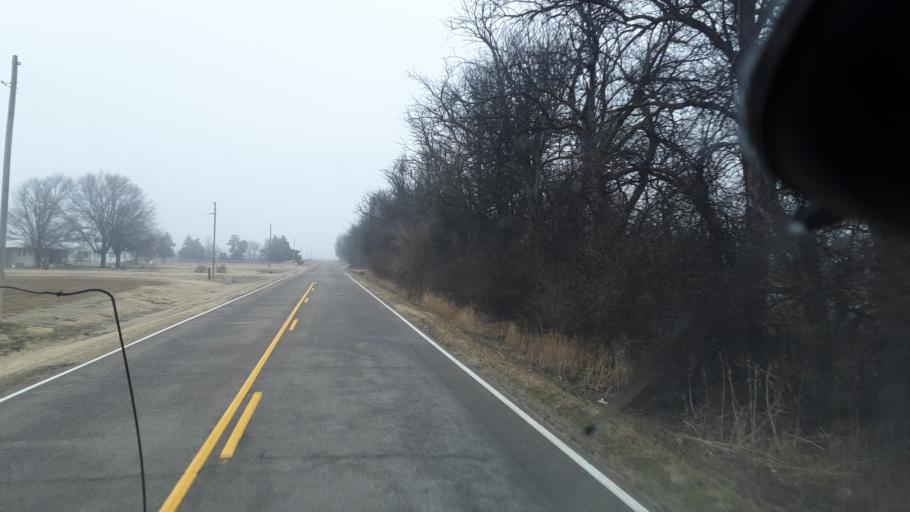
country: US
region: Kansas
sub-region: Reno County
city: South Hutchinson
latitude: 37.9504
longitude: -98.0138
